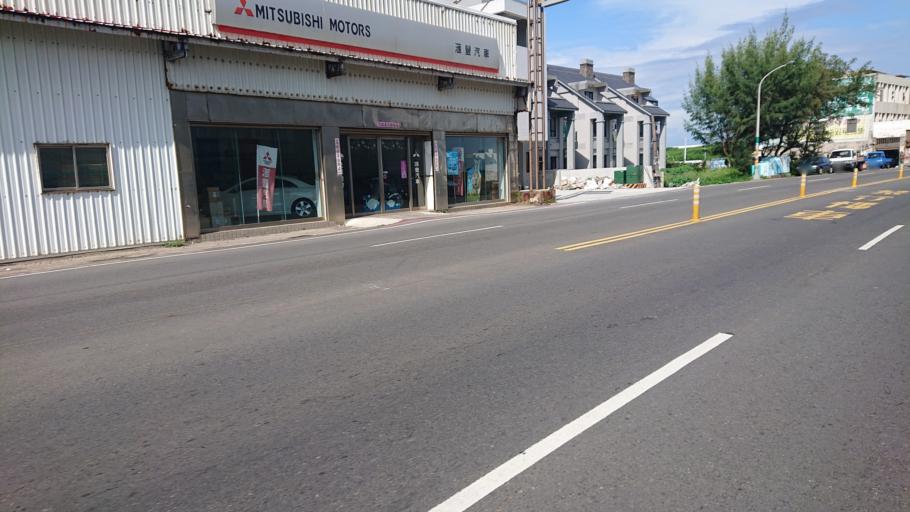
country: TW
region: Taiwan
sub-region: Penghu
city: Ma-kung
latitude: 23.5624
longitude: 119.5923
